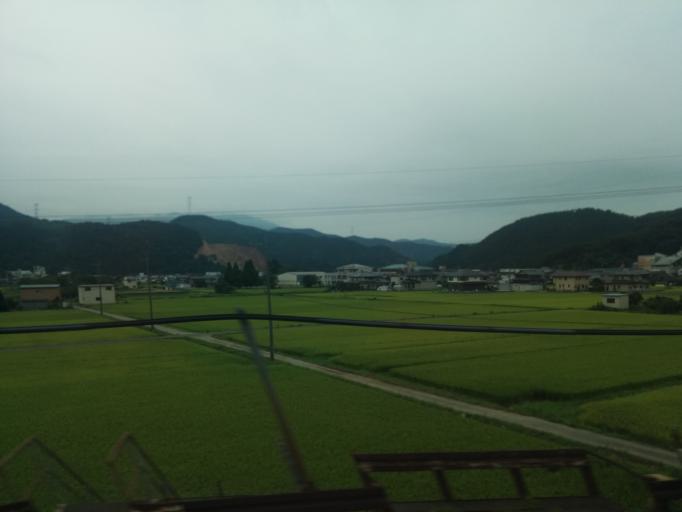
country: JP
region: Shiga Prefecture
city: Nagahama
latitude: 35.3672
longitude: 136.3716
